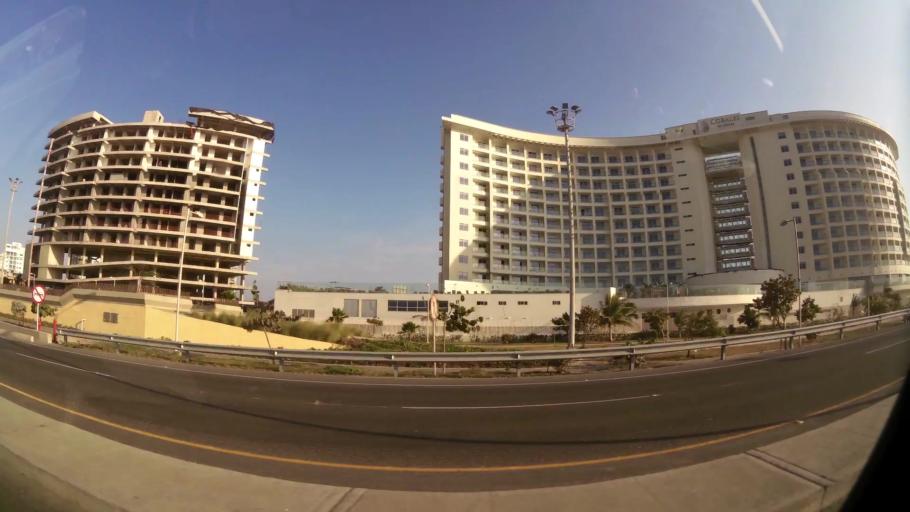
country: CO
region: Bolivar
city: Cartagena
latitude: 10.4442
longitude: -75.5256
